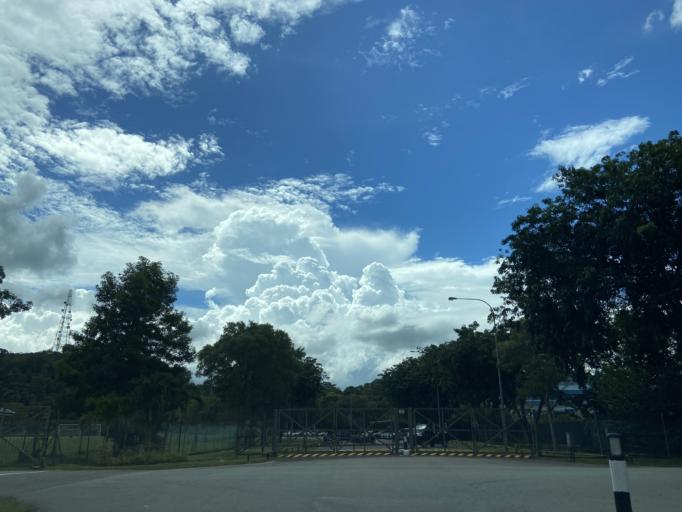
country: SG
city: Singapore
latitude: 1.0619
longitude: 104.0265
